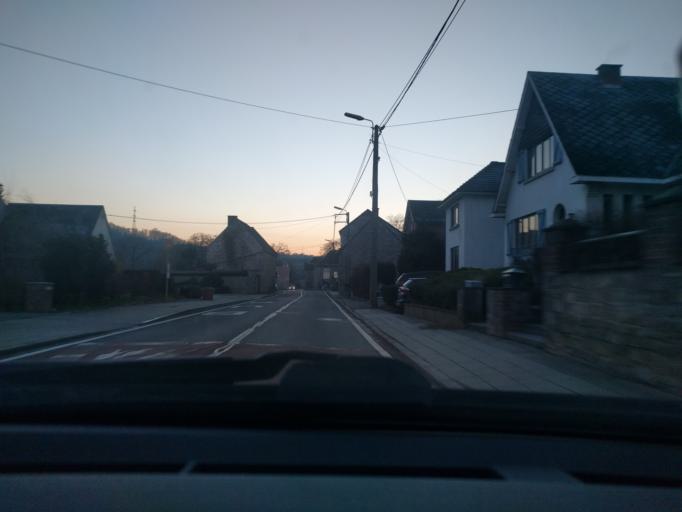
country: BE
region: Wallonia
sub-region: Province de Namur
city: Namur
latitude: 50.4687
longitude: 4.9242
